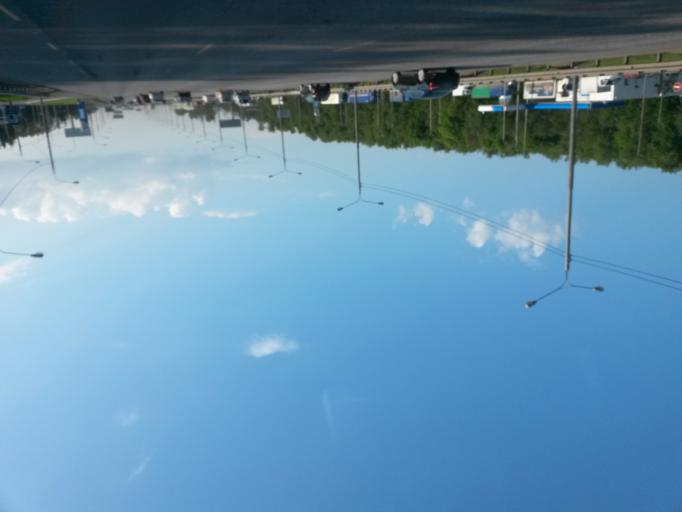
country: RU
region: Moskovskaya
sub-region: Podol'skiy Rayon
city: Podol'sk
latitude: 55.4239
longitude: 37.6123
